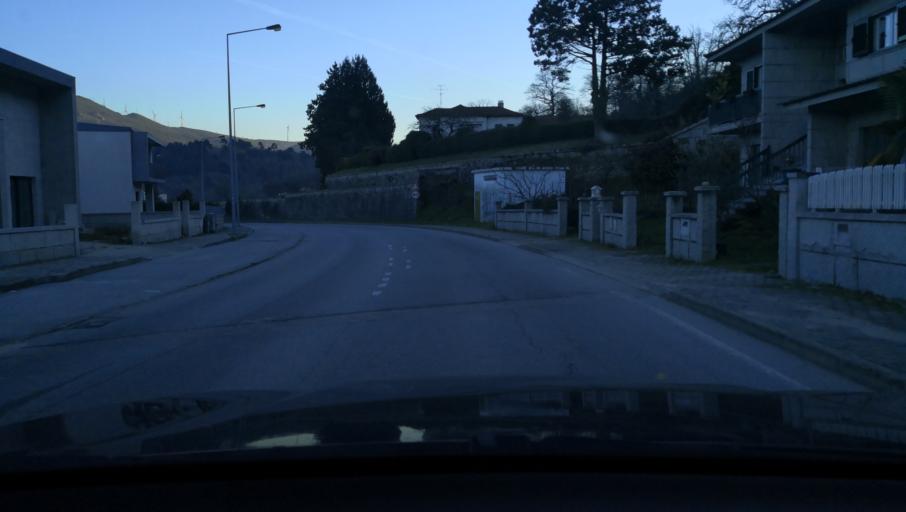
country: PT
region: Vila Real
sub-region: Vila Pouca de Aguiar
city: Vila Pouca de Aguiar
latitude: 41.4917
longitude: -7.6501
